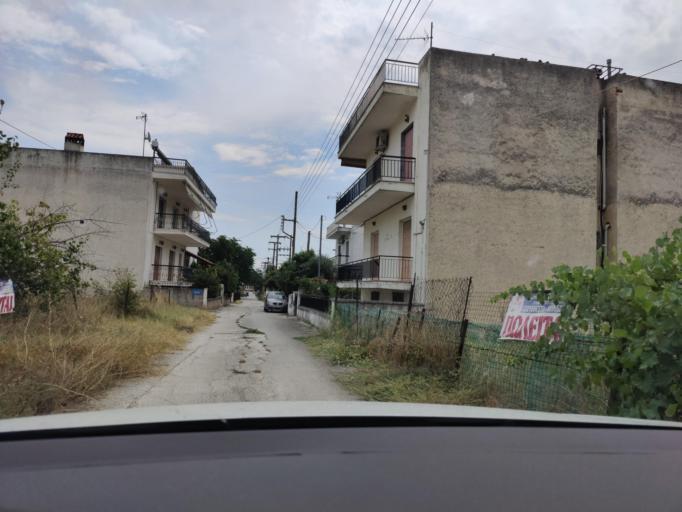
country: GR
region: Central Macedonia
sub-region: Nomos Serron
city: Serres
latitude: 41.0796
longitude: 23.5365
